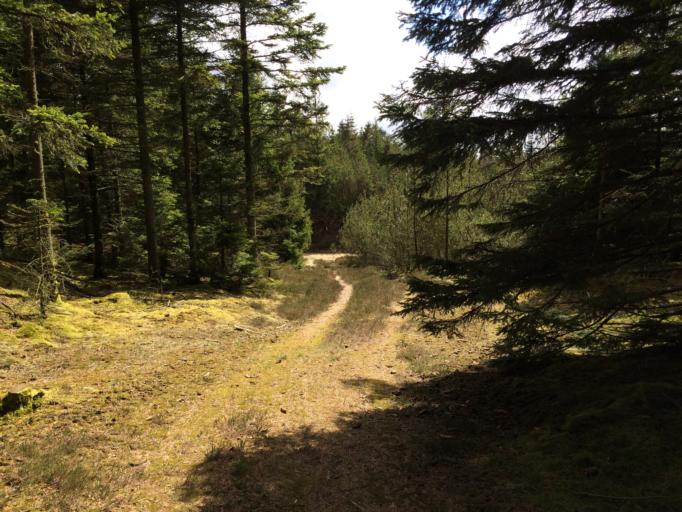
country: DK
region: Central Jutland
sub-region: Holstebro Kommune
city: Ulfborg
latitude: 56.2508
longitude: 8.4263
